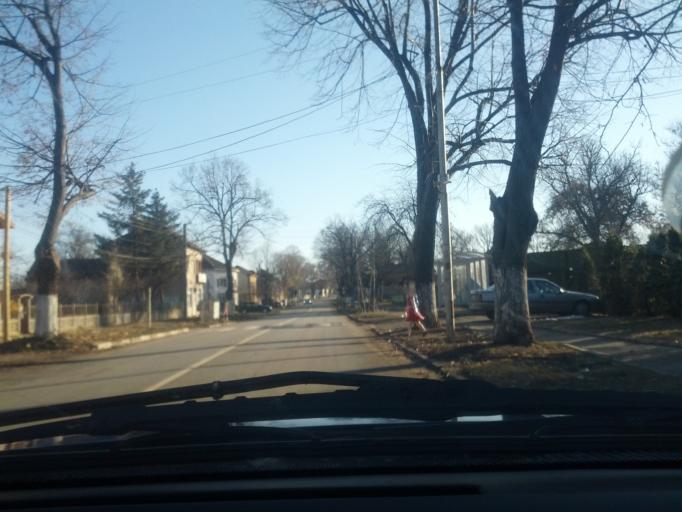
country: BG
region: Vratsa
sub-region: Obshtina Kozloduy
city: Kozloduy
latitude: 43.7729
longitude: 23.7376
